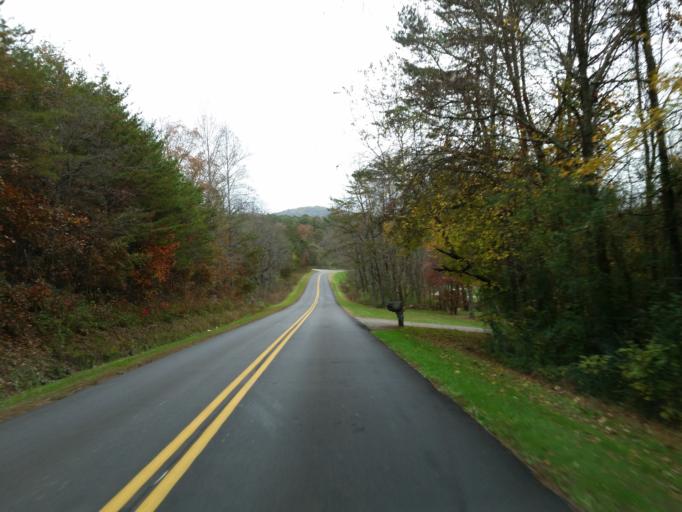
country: US
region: Georgia
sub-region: Gilmer County
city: Ellijay
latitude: 34.6493
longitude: -84.3120
